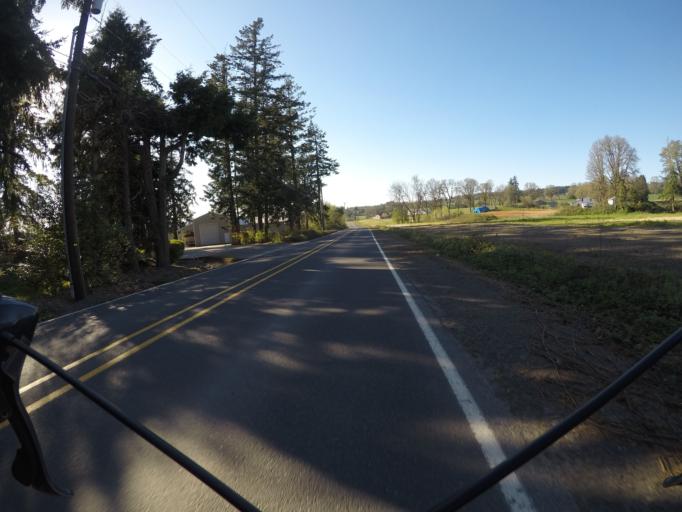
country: US
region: Oregon
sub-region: Washington County
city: Aloha
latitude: 45.4301
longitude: -122.8768
